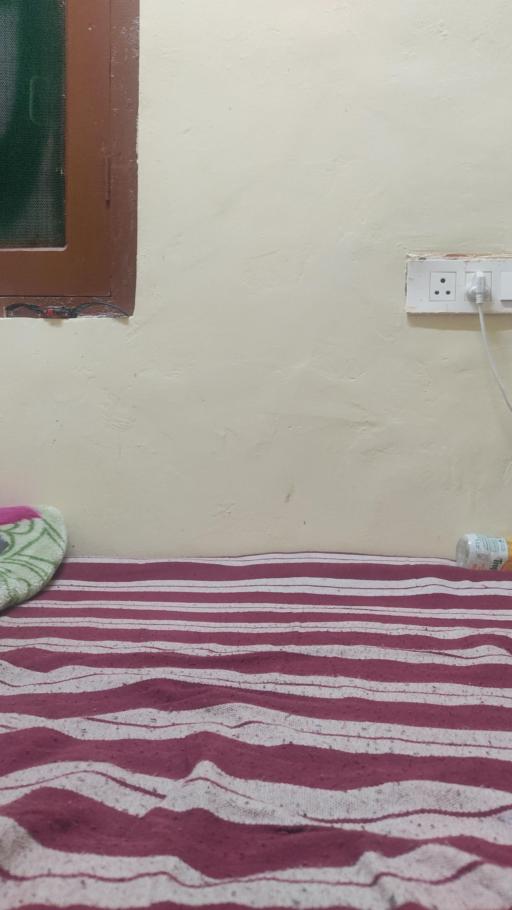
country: IN
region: Kashmir
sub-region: Anantnag
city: Qazigund
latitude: 33.6700
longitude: 75.1711
